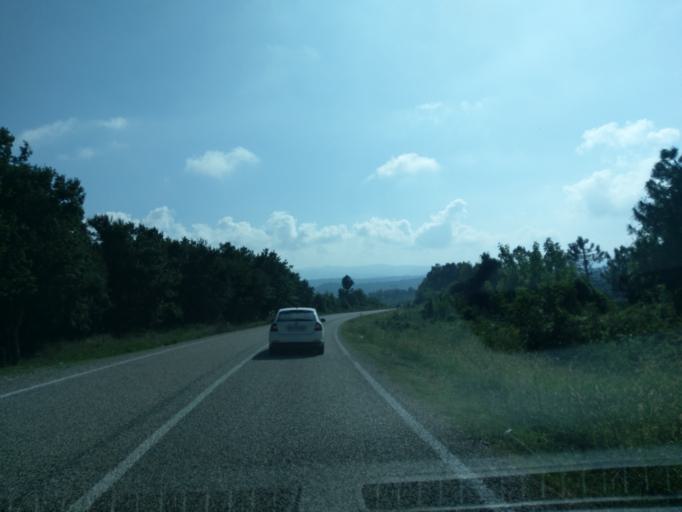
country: TR
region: Sinop
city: Erfelek
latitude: 41.9695
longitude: 34.8625
